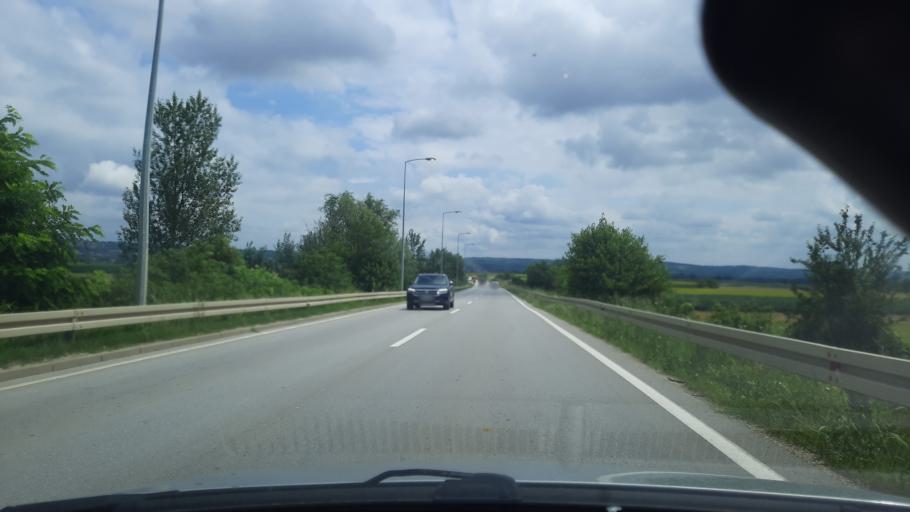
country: RS
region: Central Serbia
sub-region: Branicevski Okrug
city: Pozarevac
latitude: 44.5967
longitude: 21.1567
